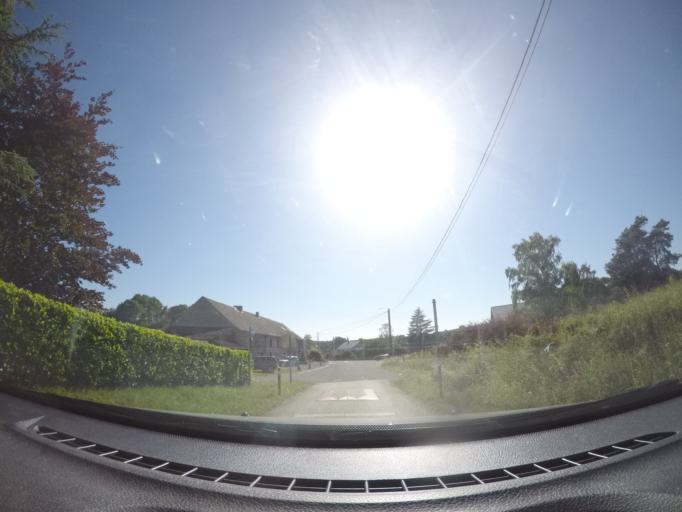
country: BE
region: Wallonia
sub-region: Province de Namur
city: Philippeville
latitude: 50.1735
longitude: 4.5637
